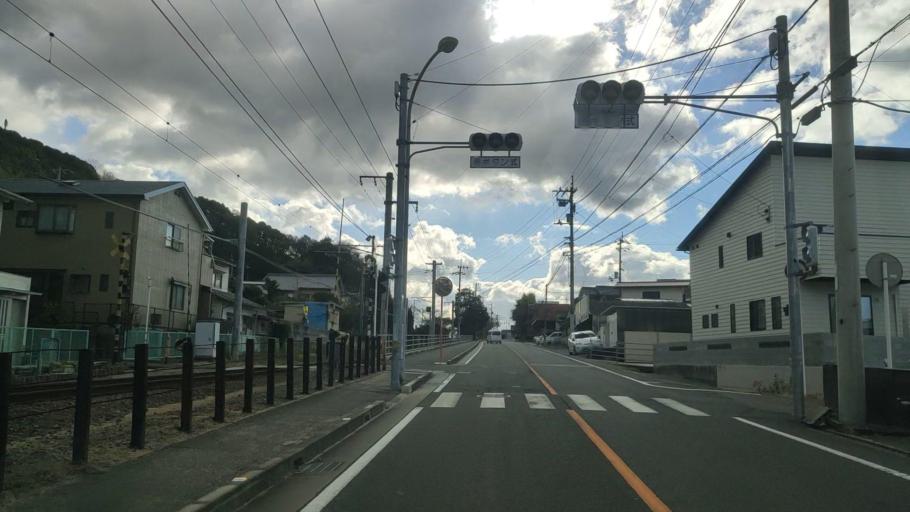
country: JP
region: Ehime
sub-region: Shikoku-chuo Shi
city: Matsuyama
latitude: 33.8800
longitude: 132.7025
